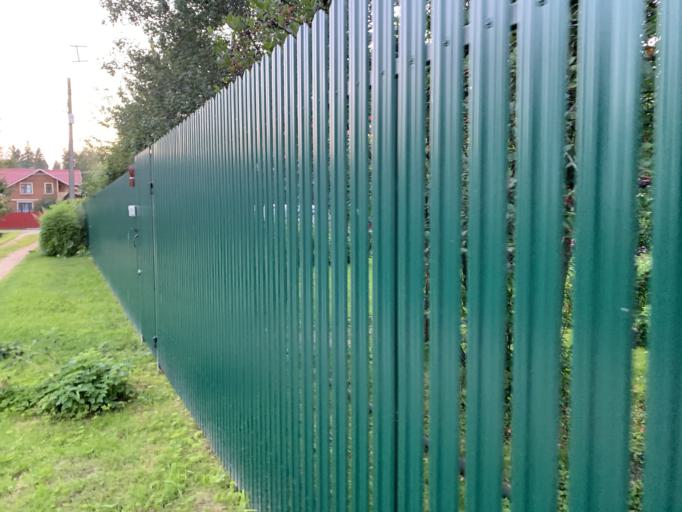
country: RU
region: Moskovskaya
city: Podosinki
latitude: 56.1762
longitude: 37.5810
